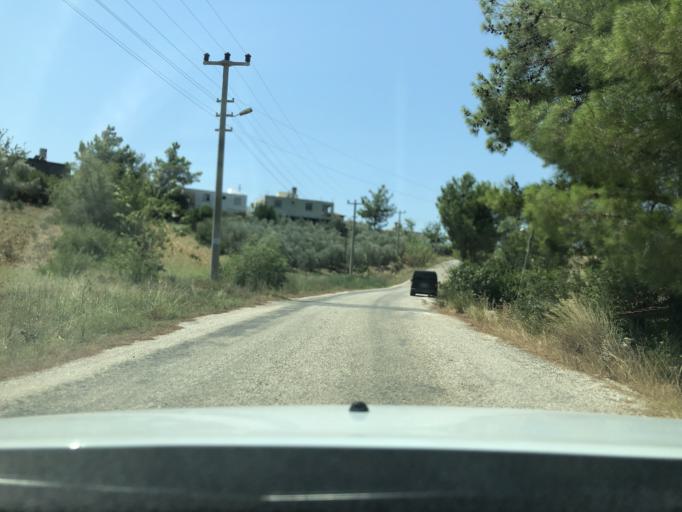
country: TR
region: Antalya
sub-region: Manavgat
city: Kizilagac
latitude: 36.8566
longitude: 31.5602
